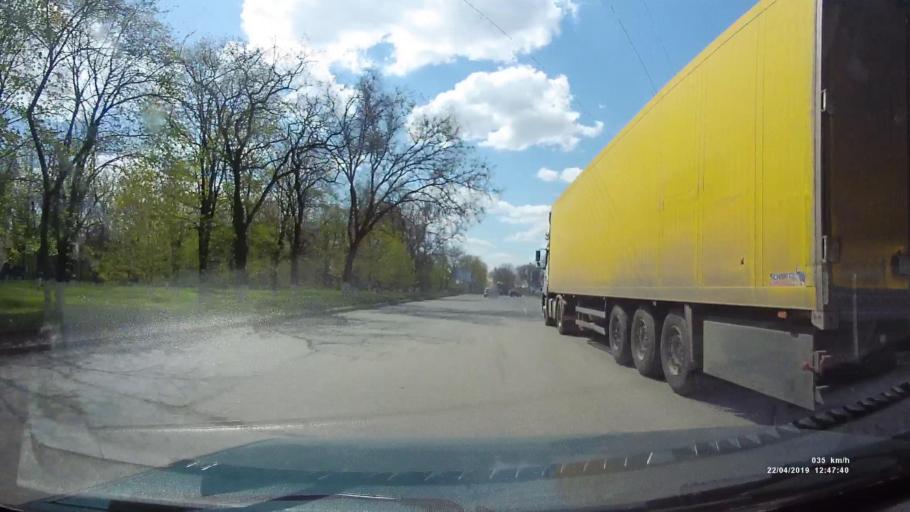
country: RU
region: Rostov
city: Azov
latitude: 47.0979
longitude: 39.4092
